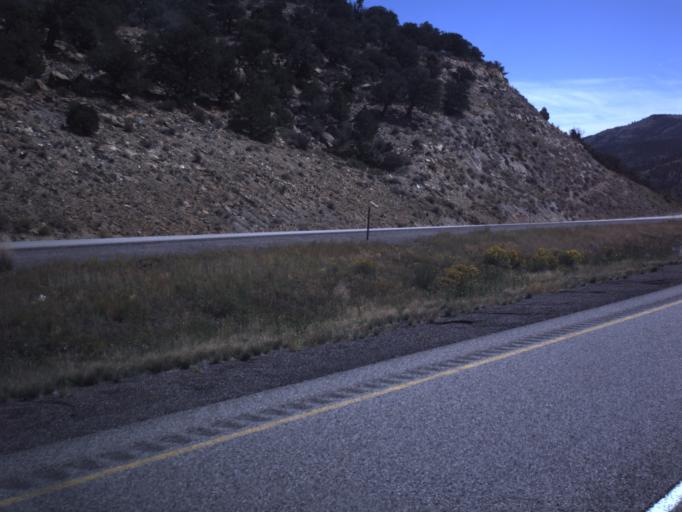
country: US
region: Utah
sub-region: Wayne County
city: Loa
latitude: 38.7677
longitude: -111.4710
